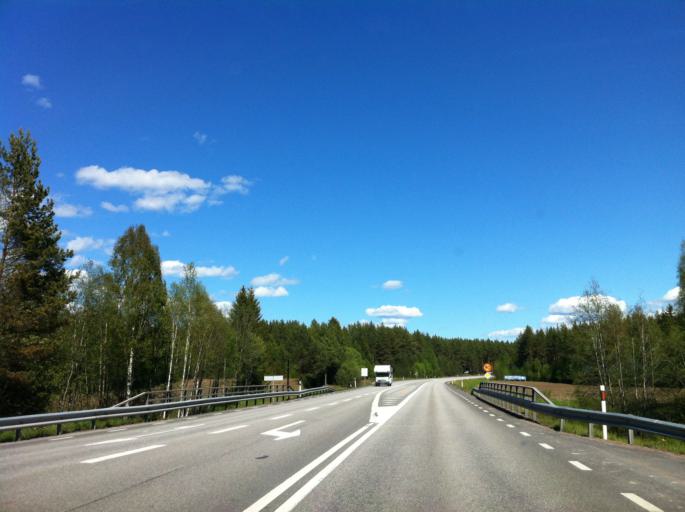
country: SE
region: Dalarna
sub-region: Rattviks Kommun
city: Vikarbyn
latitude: 60.9060
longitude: 14.9598
